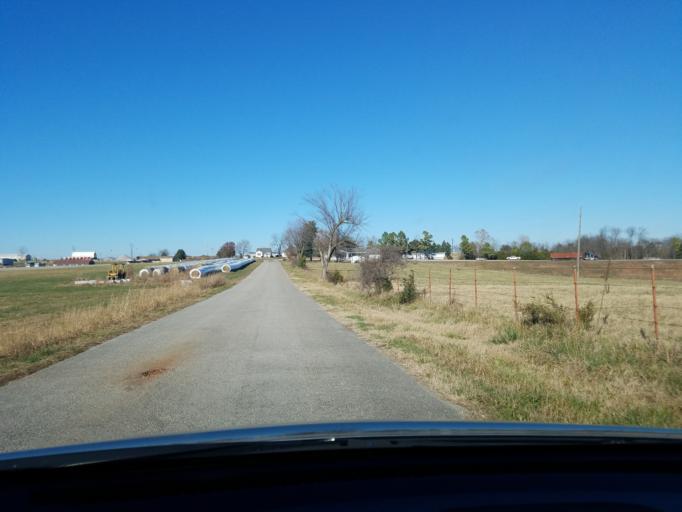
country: US
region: Arkansas
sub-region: Carroll County
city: Berryville
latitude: 36.3874
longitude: -93.6173
